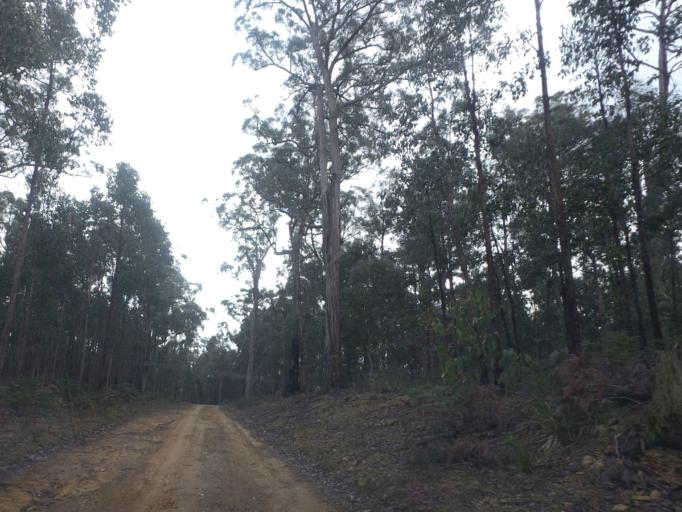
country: AU
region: Victoria
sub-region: Moorabool
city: Bacchus Marsh
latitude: -37.4486
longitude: 144.3262
